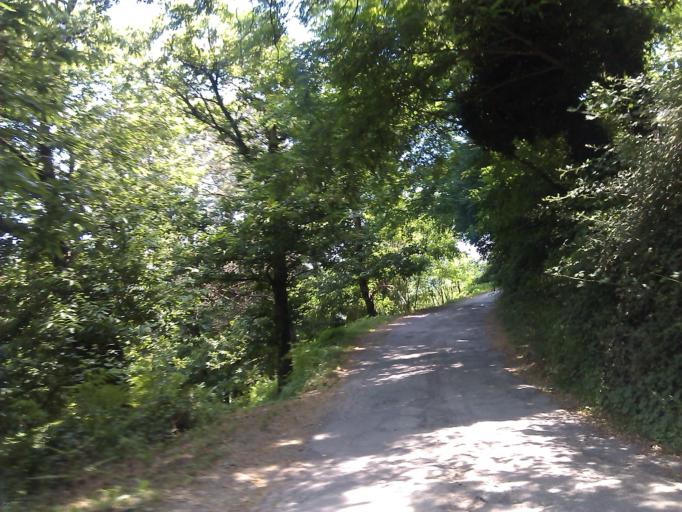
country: IT
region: Tuscany
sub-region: Provincia di Prato
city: Montemurlo
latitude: 43.9673
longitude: 11.0425
